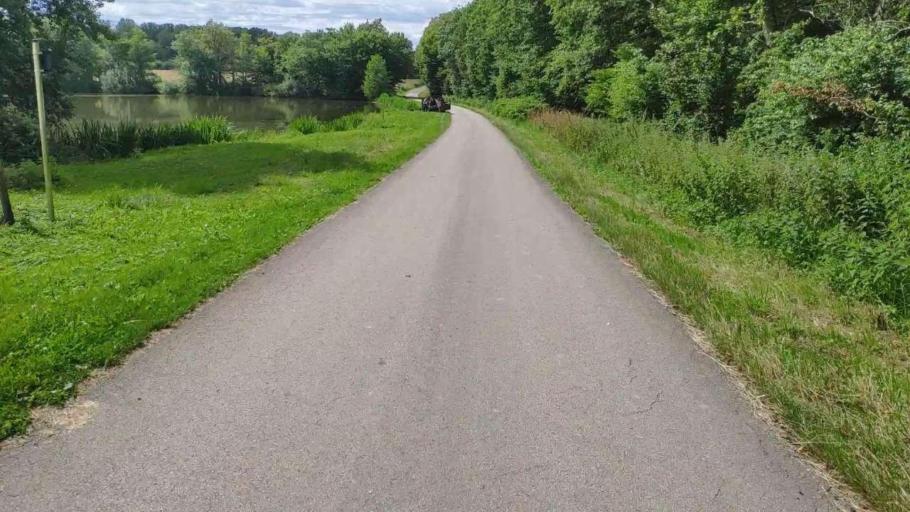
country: FR
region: Franche-Comte
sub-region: Departement du Jura
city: Bletterans
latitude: 46.8066
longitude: 5.4446
